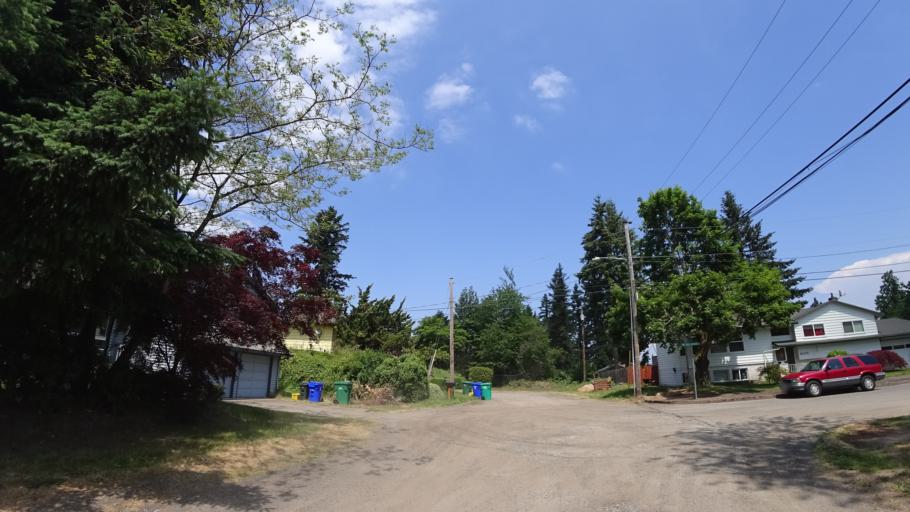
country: US
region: Oregon
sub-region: Multnomah County
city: Fairview
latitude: 45.5315
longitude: -122.4973
